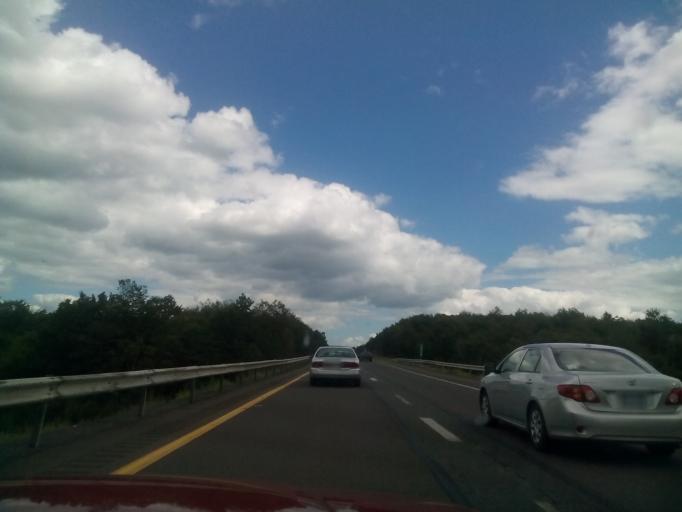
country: US
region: Pennsylvania
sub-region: Monroe County
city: Emerald Lakes
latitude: 41.0713
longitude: -75.4150
